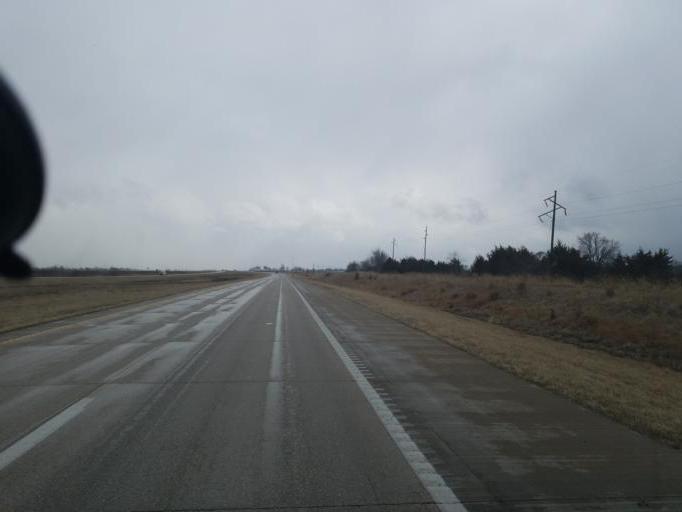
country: US
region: Missouri
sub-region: Randolph County
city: Moberly
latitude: 39.5360
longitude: -92.4474
